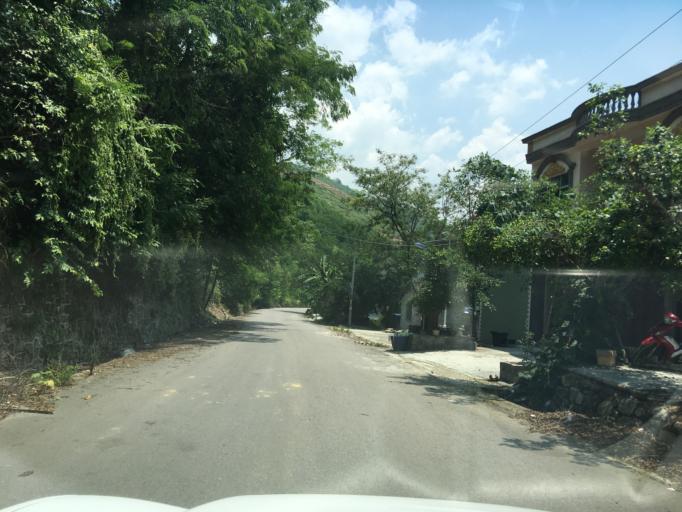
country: CN
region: Guangxi Zhuangzu Zizhiqu
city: Xinzhou
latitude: 24.9152
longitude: 105.4478
